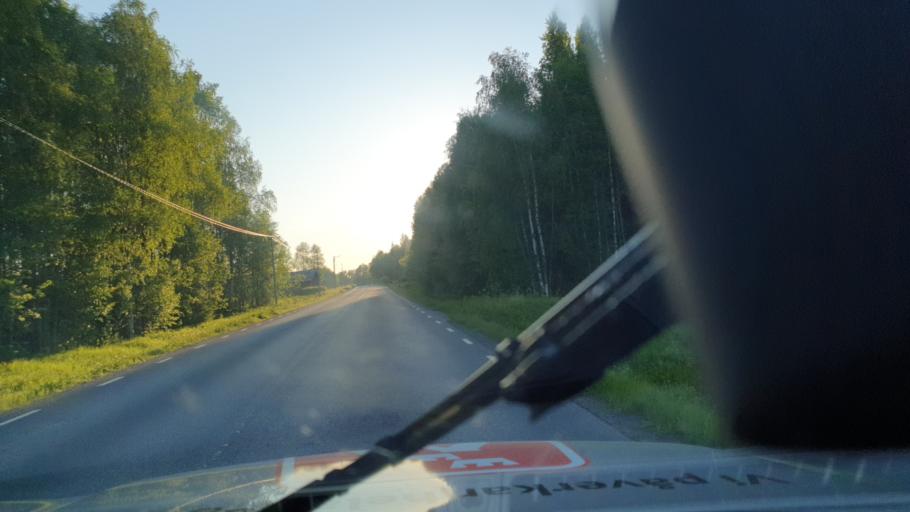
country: SE
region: Norrbotten
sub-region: Lulea Kommun
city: Gammelstad
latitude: 65.7984
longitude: 22.0600
